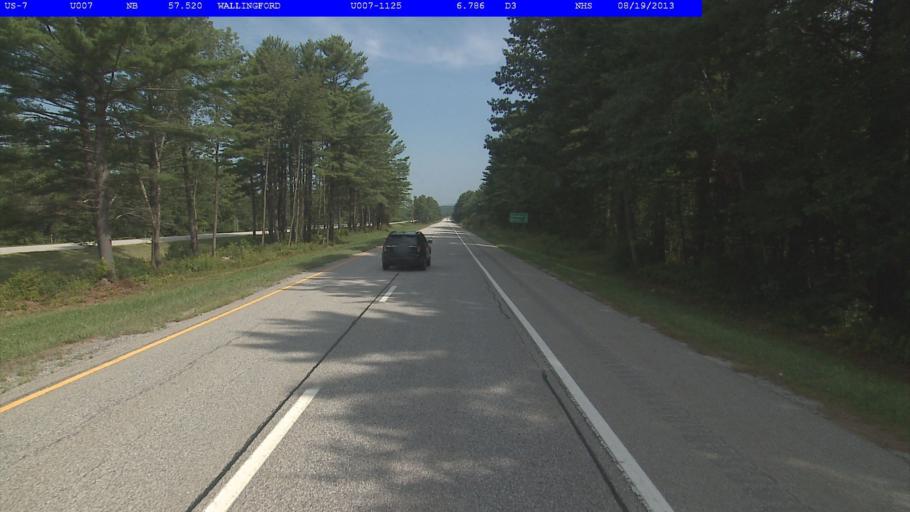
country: US
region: Vermont
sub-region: Rutland County
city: Rutland
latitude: 43.4896
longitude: -72.9702
